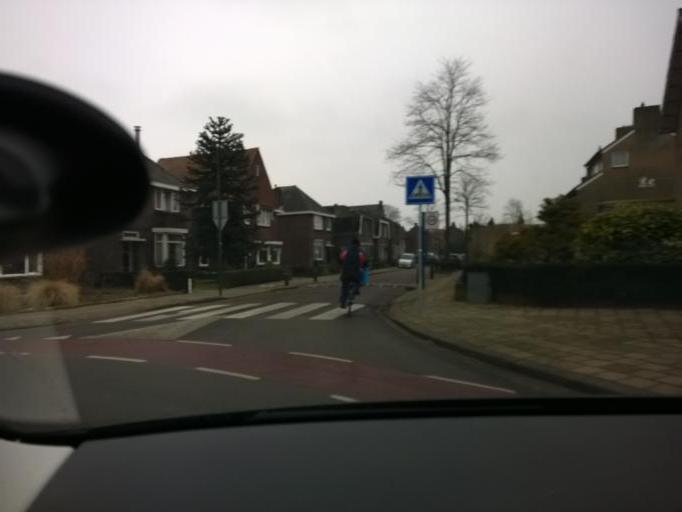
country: NL
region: North Brabant
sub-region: Gemeente Veldhoven
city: Veldhoven
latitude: 51.4195
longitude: 5.4188
